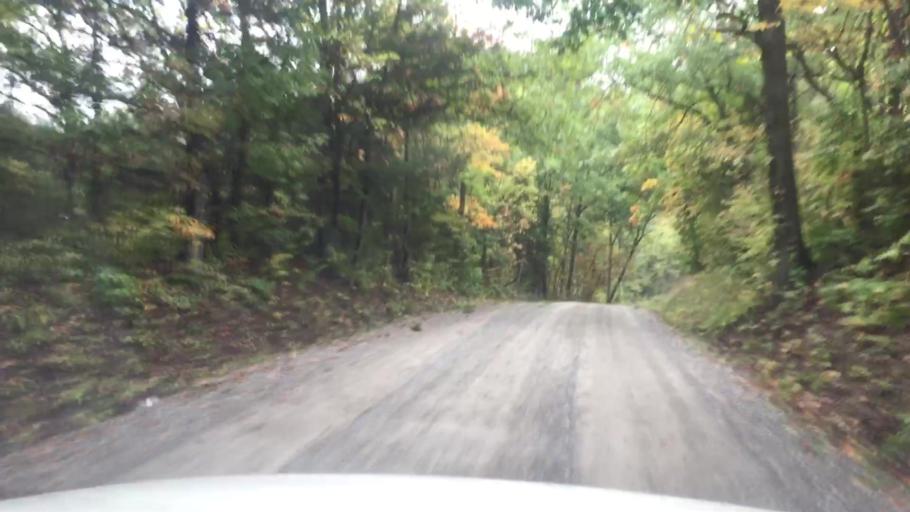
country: US
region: Missouri
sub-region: Boone County
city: Ashland
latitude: 38.8187
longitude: -92.3115
